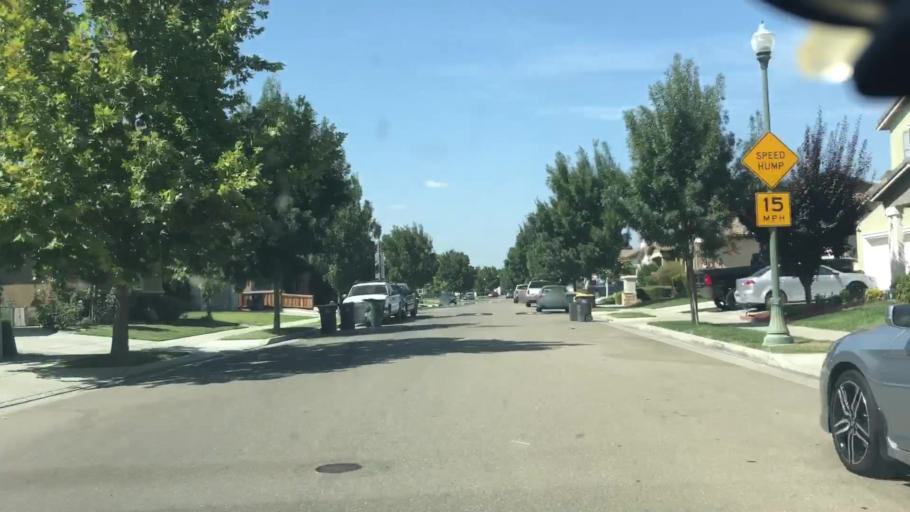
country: US
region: California
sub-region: San Joaquin County
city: Lathrop
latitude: 37.8156
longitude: -121.3089
